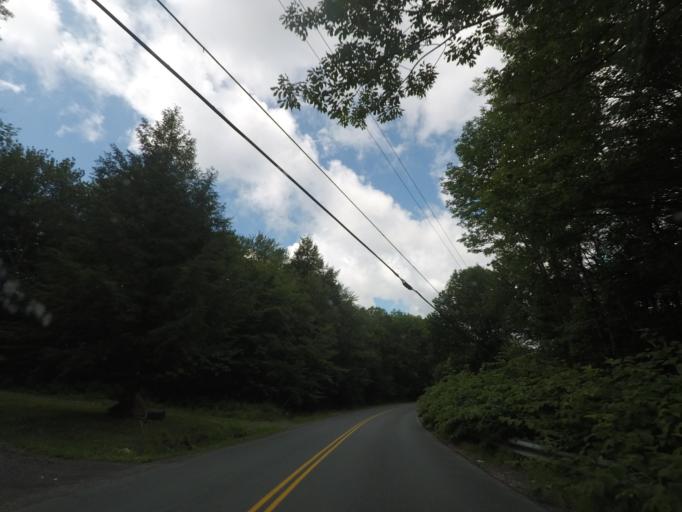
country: US
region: New York
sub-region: Rensselaer County
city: Averill Park
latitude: 42.6413
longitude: -73.4713
